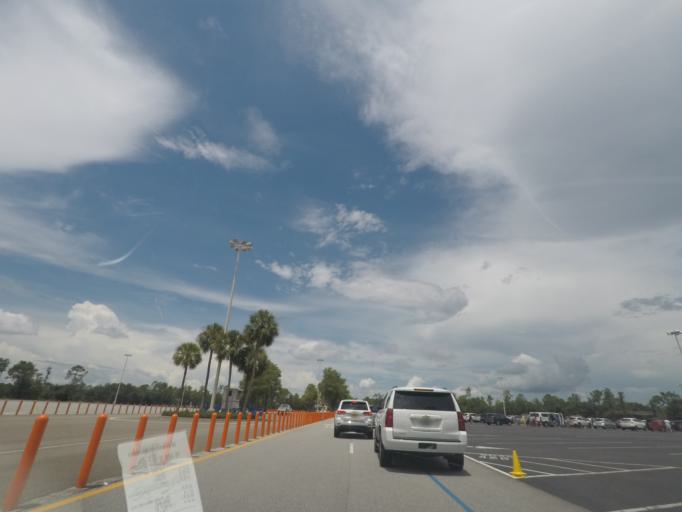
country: US
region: Florida
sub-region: Osceola County
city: Celebration
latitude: 28.3995
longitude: -81.5761
